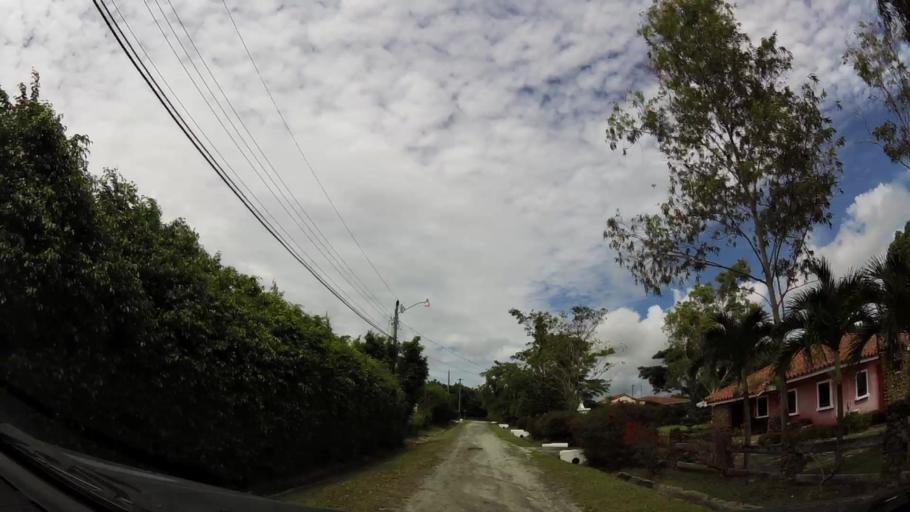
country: PA
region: Panama
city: Nueva Gorgona
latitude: 8.5387
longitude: -79.9059
